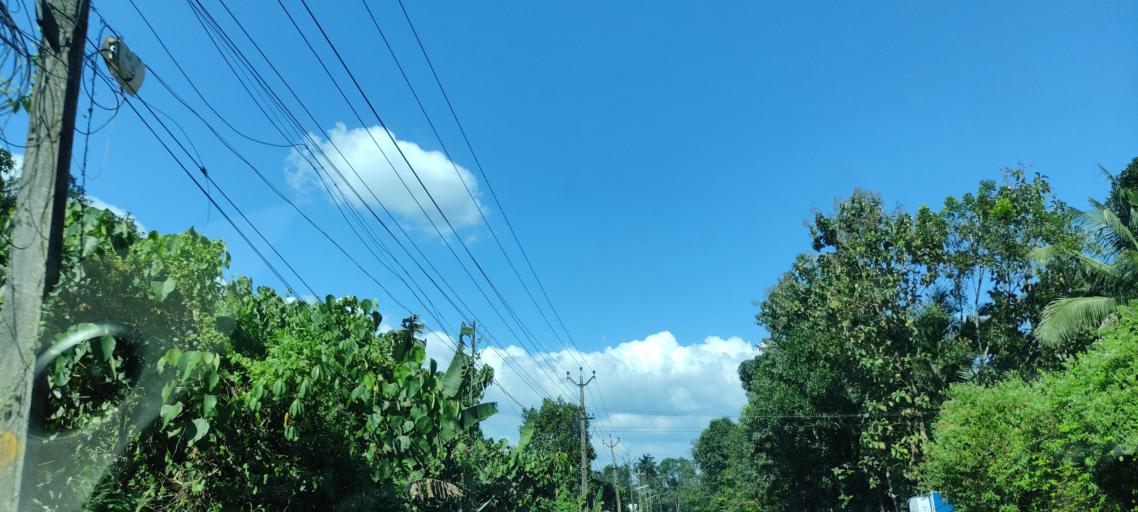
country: IN
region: Kerala
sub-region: Pattanamtitta
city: Adur
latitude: 9.1772
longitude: 76.7418
